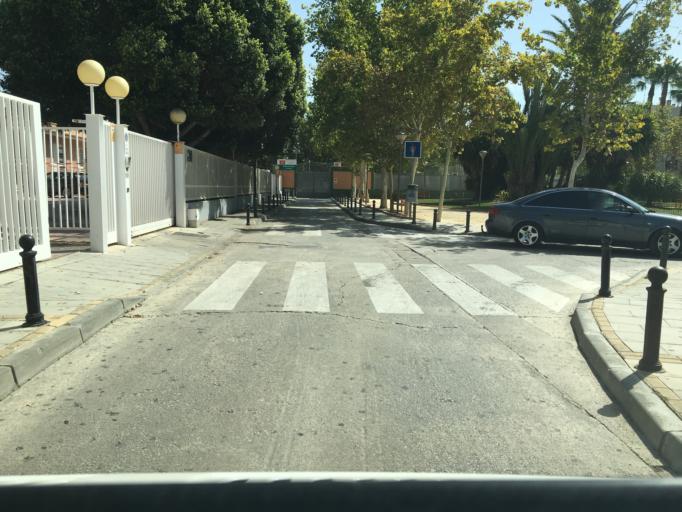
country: ES
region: Murcia
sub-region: Murcia
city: Murcia
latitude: 37.9967
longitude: -1.1226
